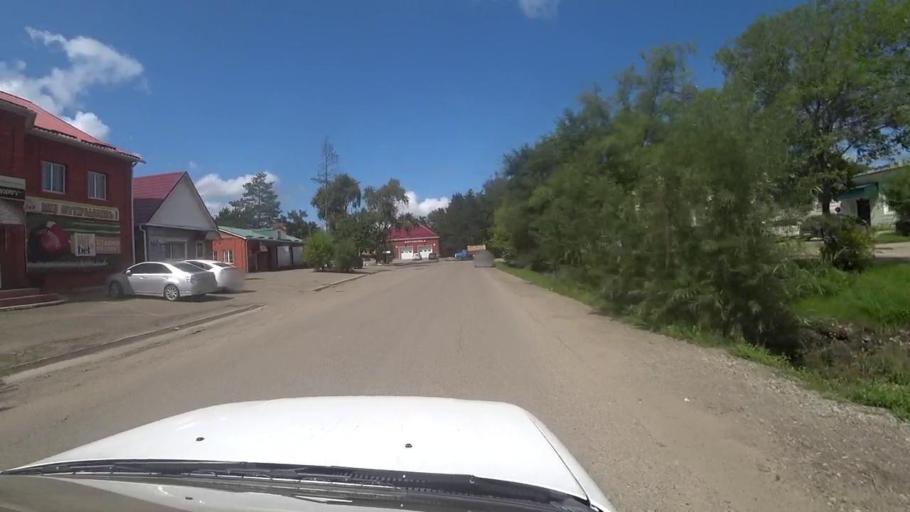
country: RU
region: Primorskiy
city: Dal'nerechensk
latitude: 45.9295
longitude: 133.7300
